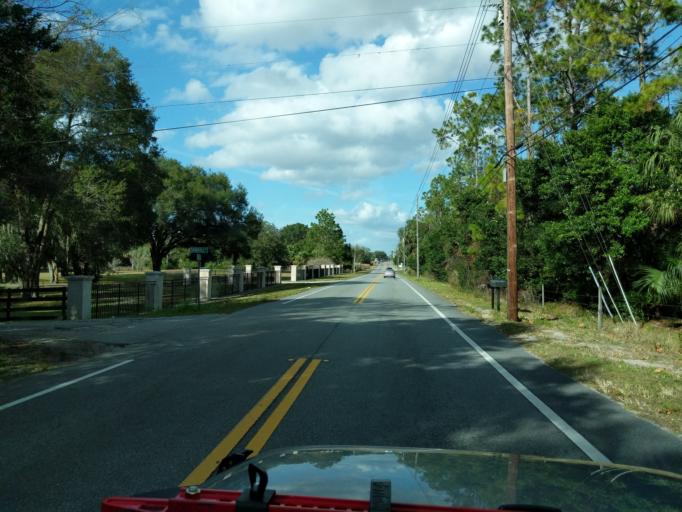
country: US
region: Florida
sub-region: Seminole County
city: Geneva
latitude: 28.7276
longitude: -81.1150
